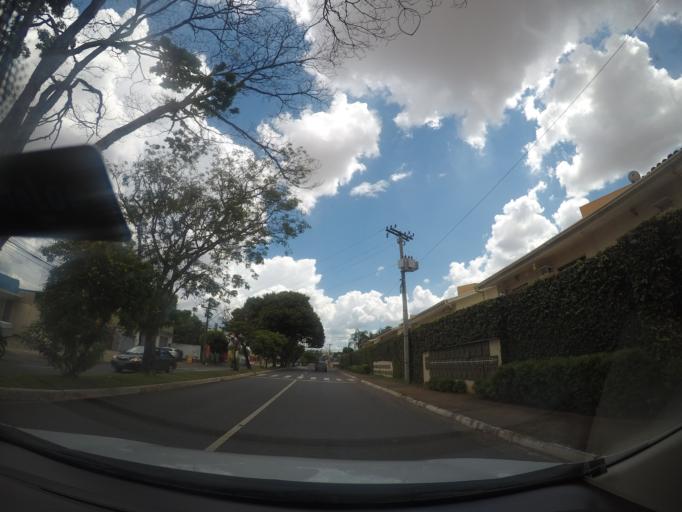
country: BR
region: Goias
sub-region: Goiania
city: Goiania
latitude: -16.6999
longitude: -49.2808
